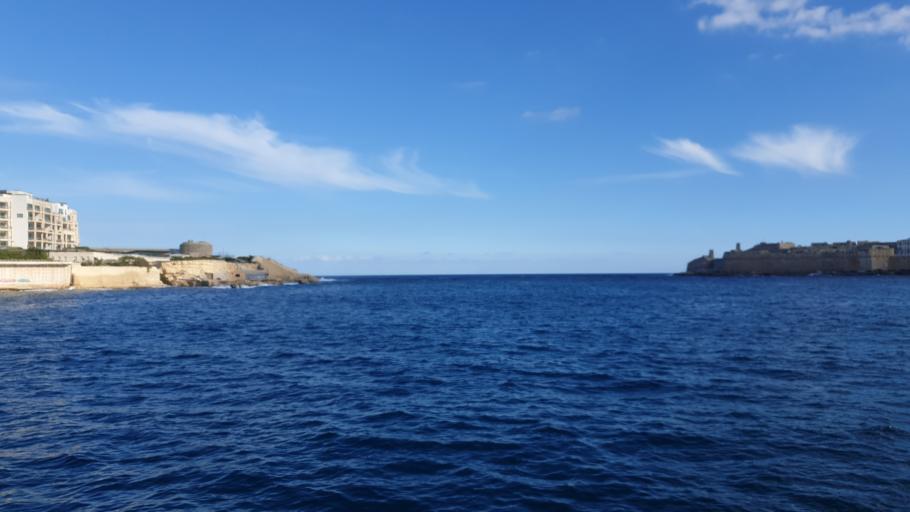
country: MT
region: Il-Belt Valletta
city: Valletta
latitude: 35.9040
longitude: 14.5093
